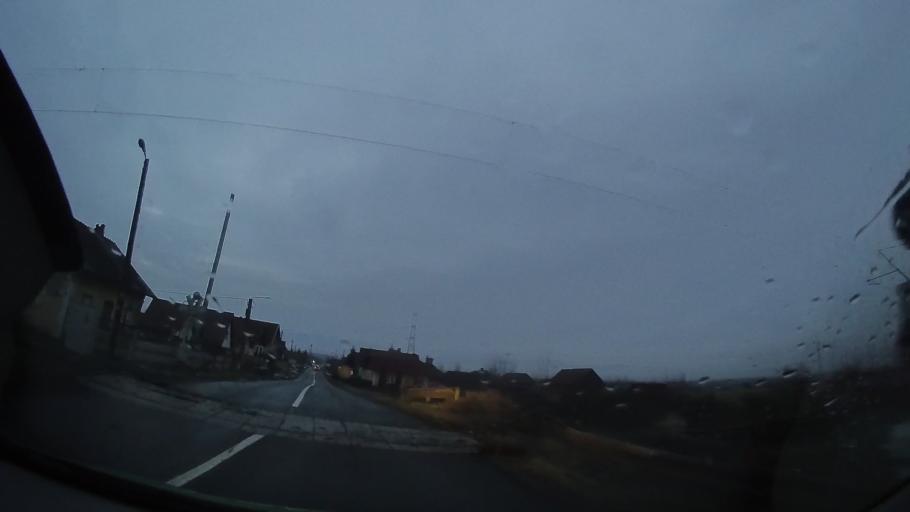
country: RO
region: Harghita
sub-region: Comuna Remetea
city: Remetea
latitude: 46.8013
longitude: 25.4752
